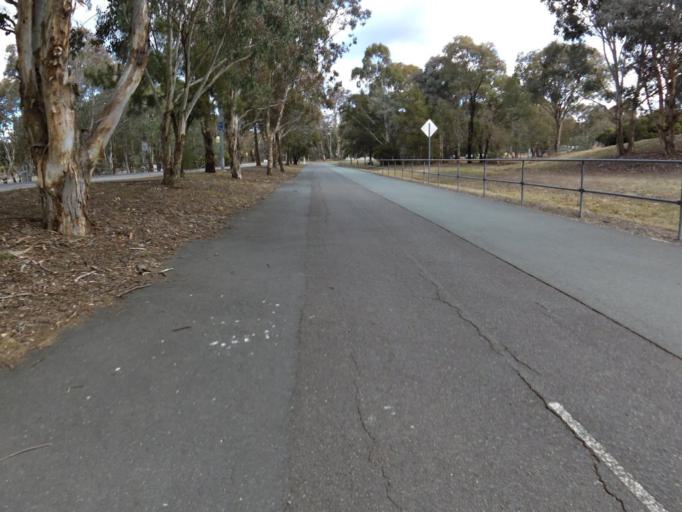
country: AU
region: Australian Capital Territory
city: Acton
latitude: -35.2494
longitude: 149.1050
